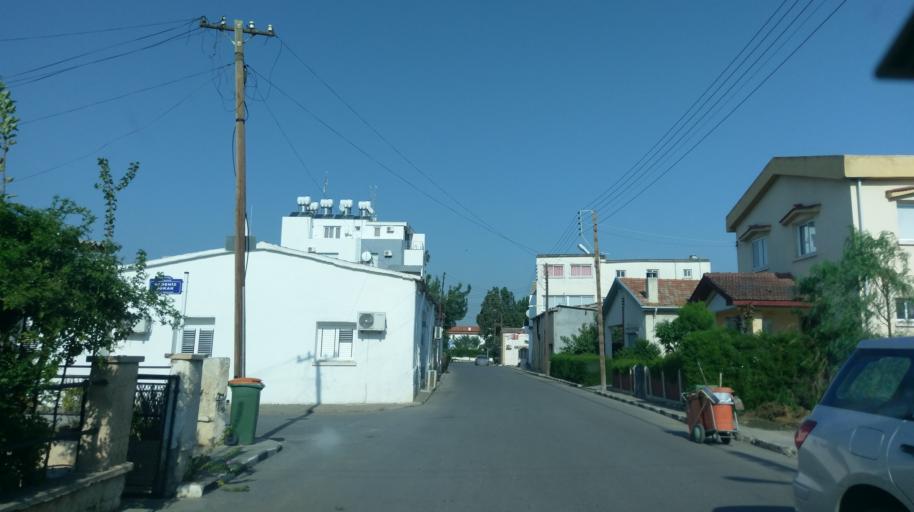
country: CY
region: Lefkosia
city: Morfou
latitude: 35.1989
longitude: 32.9893
